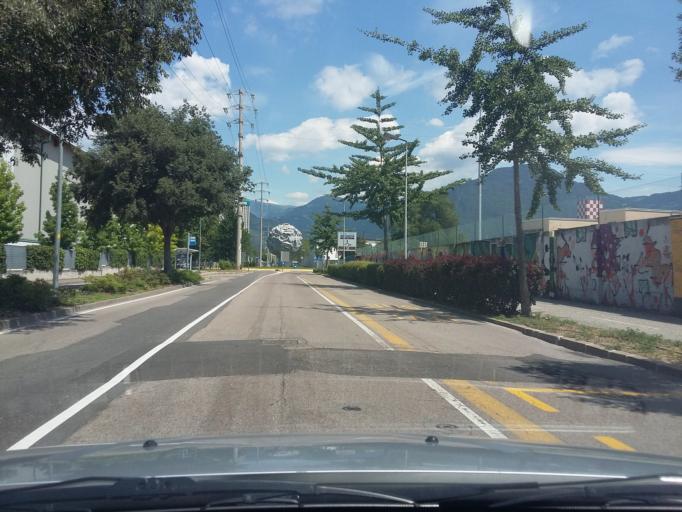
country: IT
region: Trentino-Alto Adige
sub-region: Bolzano
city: Bolzano
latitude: 46.4788
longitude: 11.3287
